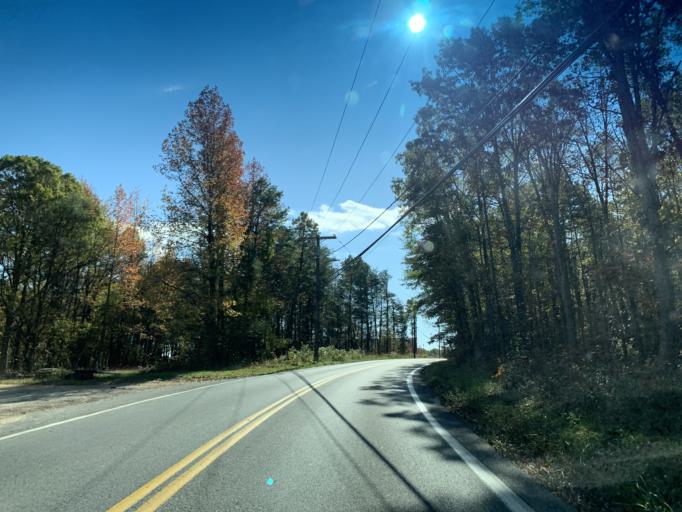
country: US
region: Maryland
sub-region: Anne Arundel County
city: Gambrills
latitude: 39.1015
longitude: -76.6532
